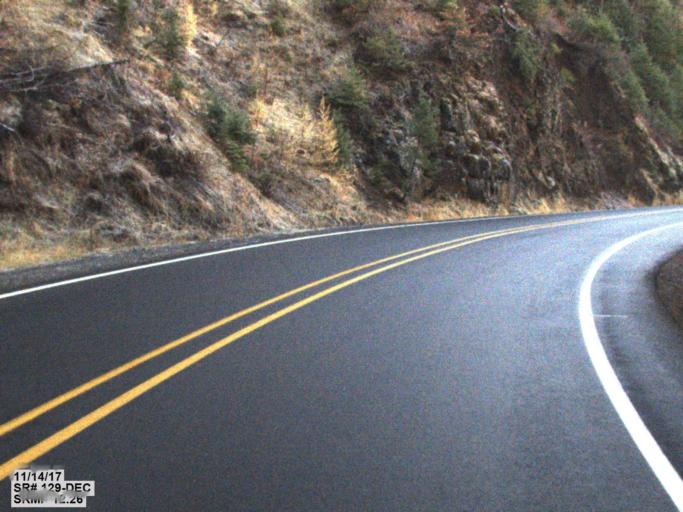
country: US
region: Washington
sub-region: Asotin County
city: Asotin
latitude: 46.0799
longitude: -117.1875
